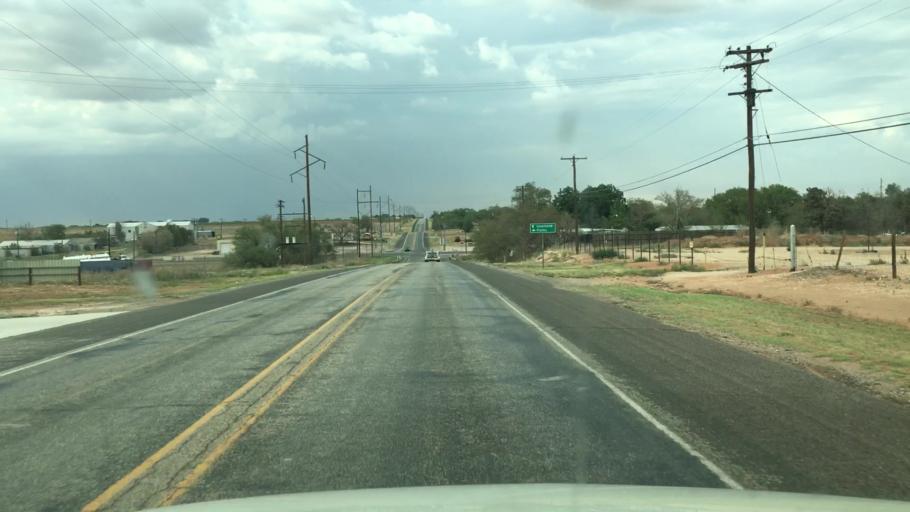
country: US
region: Texas
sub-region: Terry County
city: Brownfield
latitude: 33.1766
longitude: -102.2915
